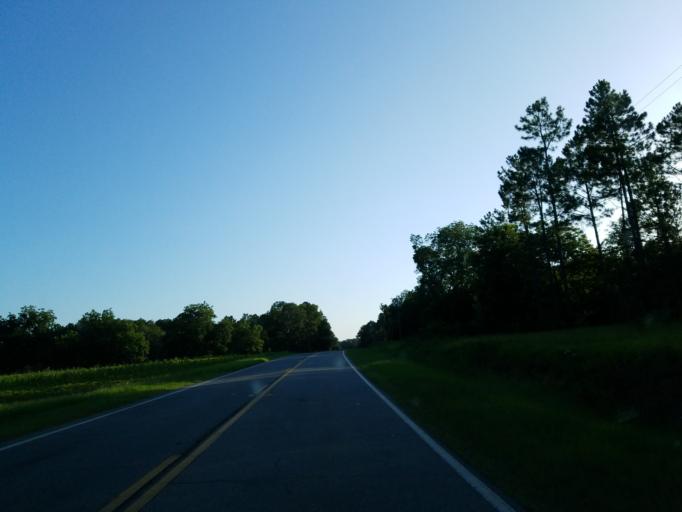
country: US
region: Georgia
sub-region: Tift County
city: Tifton
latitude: 31.5985
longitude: -83.4660
